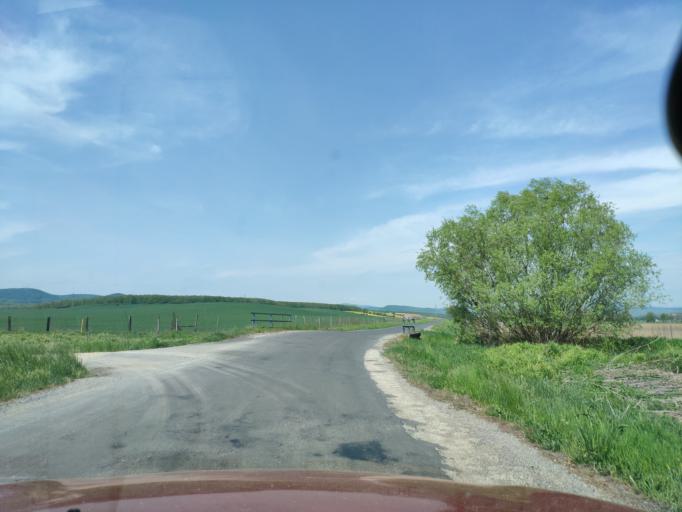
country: SK
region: Banskobystricky
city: Rimavska Sobota
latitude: 48.4171
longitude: 20.1261
